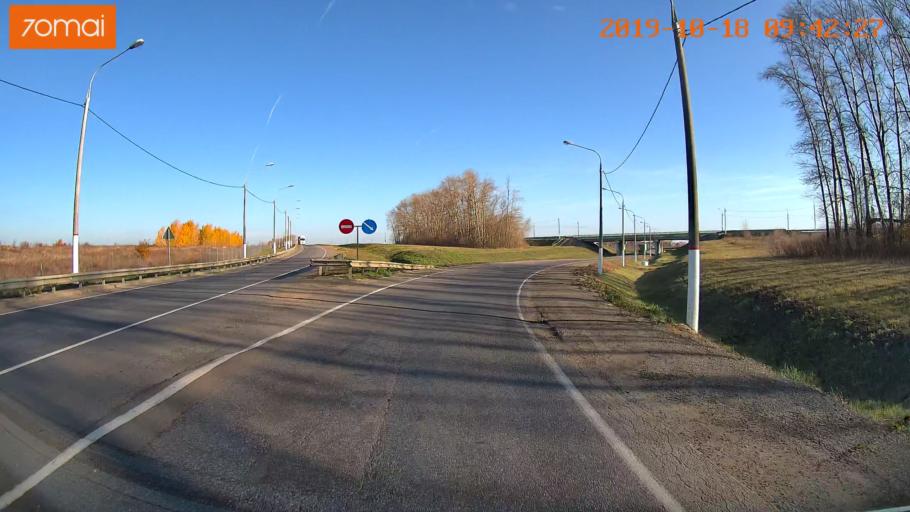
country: RU
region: Tula
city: Kazachka
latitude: 53.2872
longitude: 38.1766
